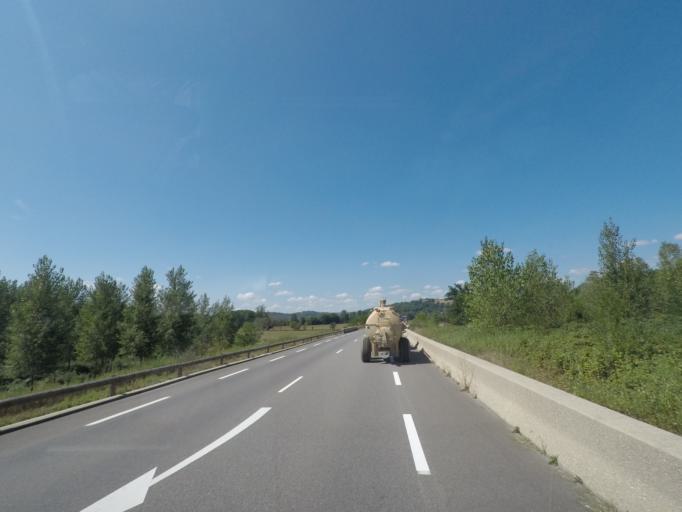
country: FR
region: Midi-Pyrenees
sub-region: Departement du Lot
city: Figeac
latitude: 44.5927
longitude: 1.9871
